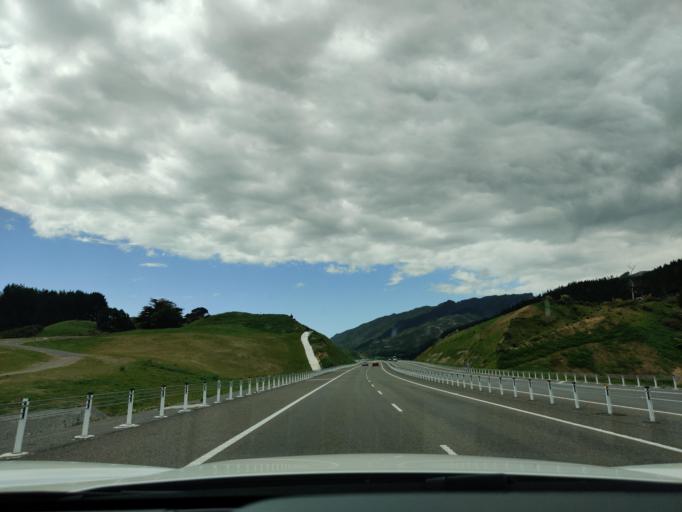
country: NZ
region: Wellington
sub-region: Porirua City
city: Porirua
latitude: -41.0660
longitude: 174.9432
